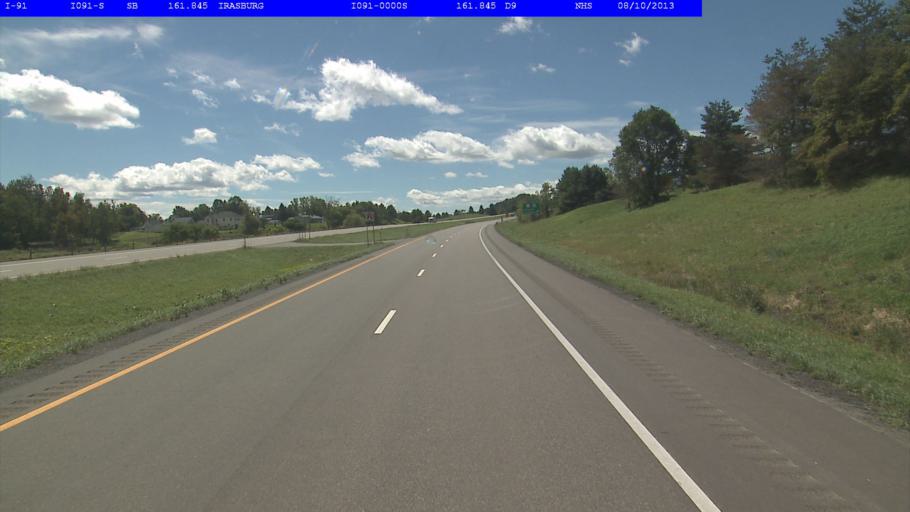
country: US
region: Vermont
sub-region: Orleans County
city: Newport
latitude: 44.8128
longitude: -72.2111
